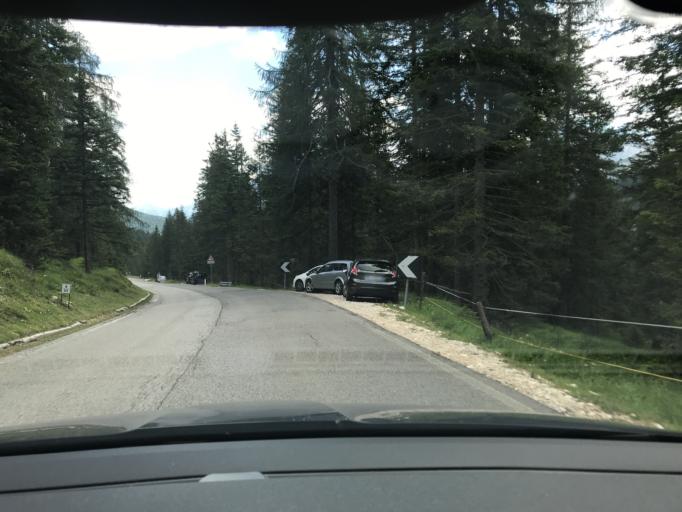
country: IT
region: Veneto
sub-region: Provincia di Belluno
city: Cortina d'Ampezzo
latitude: 46.5565
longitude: 12.2110
